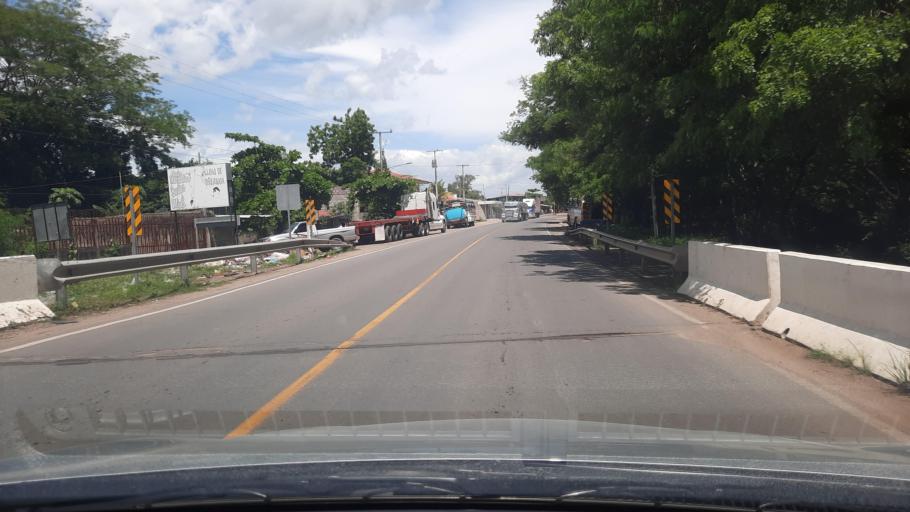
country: NI
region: Chinandega
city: Somotillo
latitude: 13.0487
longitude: -86.9045
